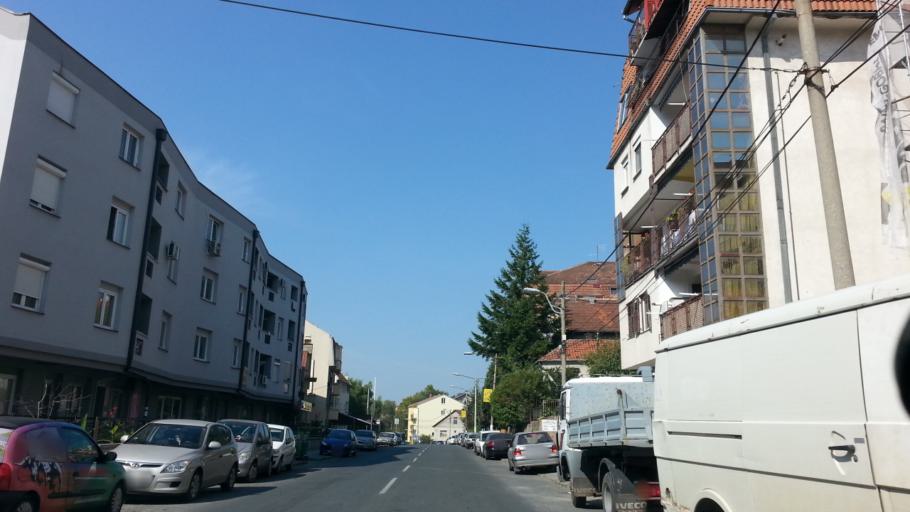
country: RS
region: Central Serbia
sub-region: Belgrade
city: Rakovica
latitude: 44.7554
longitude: 20.4219
